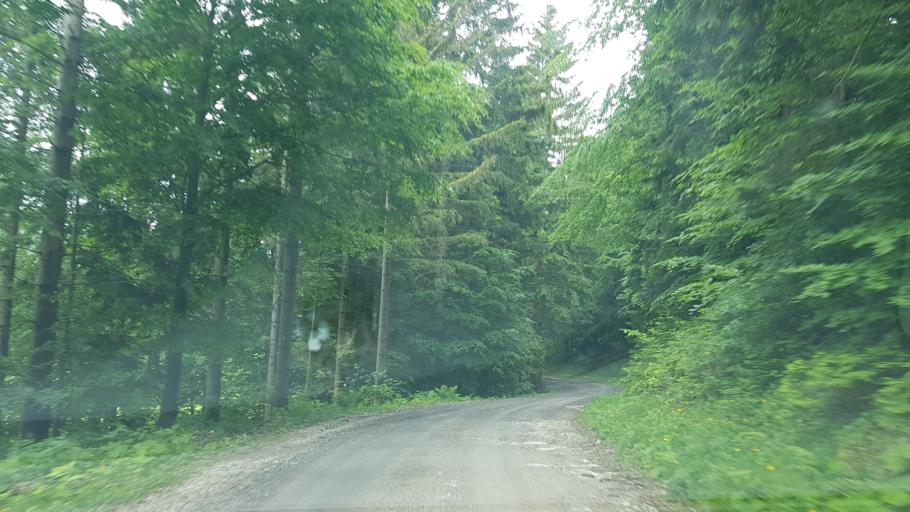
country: SI
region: Dobrna
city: Dobrna
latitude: 46.3827
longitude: 15.2250
